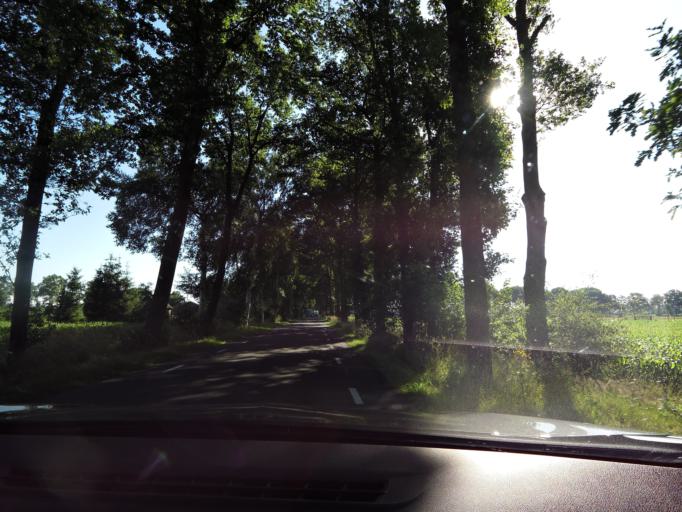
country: NL
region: Overijssel
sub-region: Gemeente Raalte
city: Raalte
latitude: 52.3077
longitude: 6.3263
